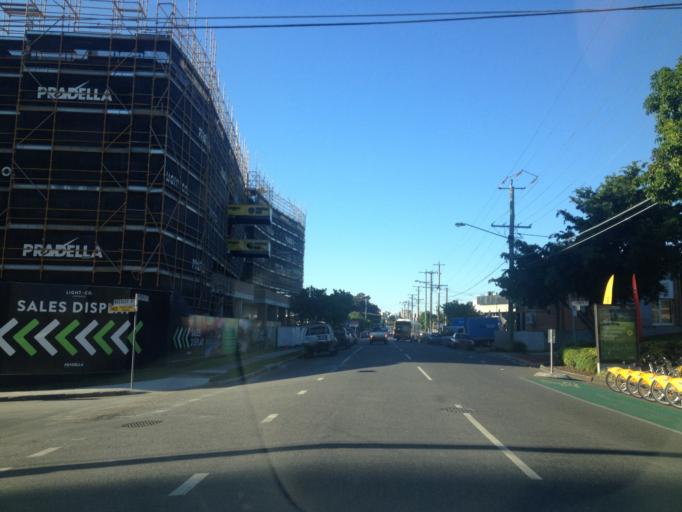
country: AU
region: Queensland
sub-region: Brisbane
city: Milton
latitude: -27.4818
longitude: 153.0041
